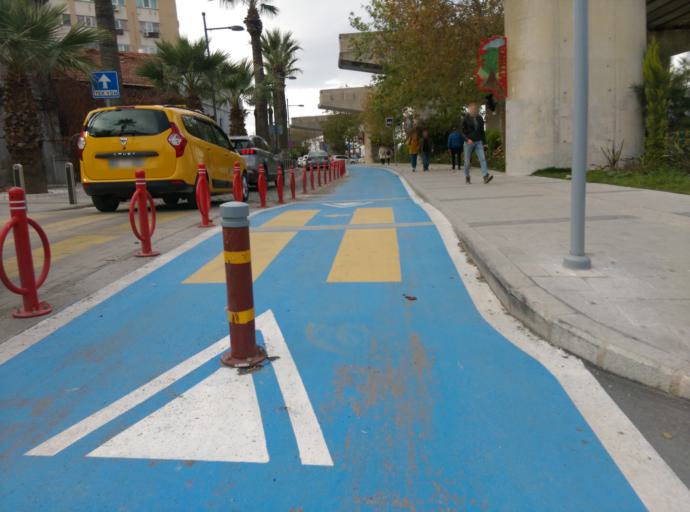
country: TR
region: Izmir
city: Izmir
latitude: 38.4418
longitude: 27.1458
